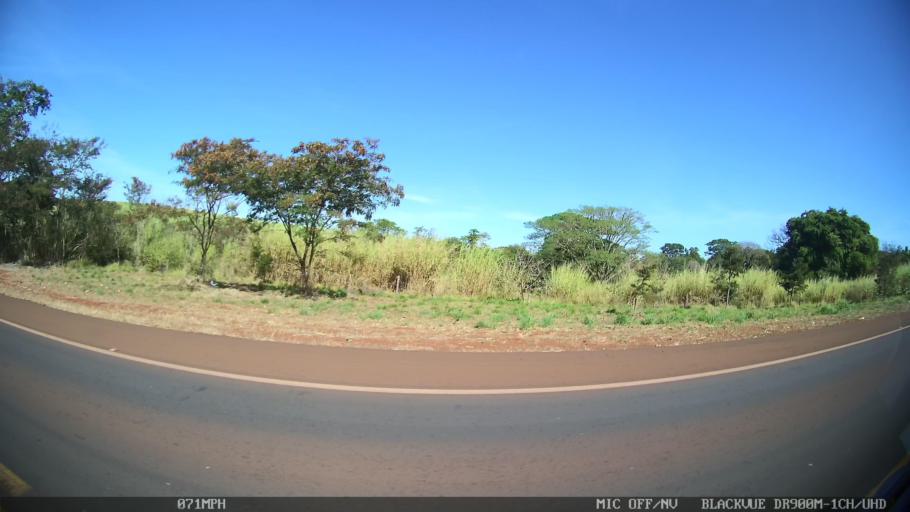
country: BR
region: Sao Paulo
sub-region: Ipua
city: Ipua
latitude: -20.4933
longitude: -48.0246
